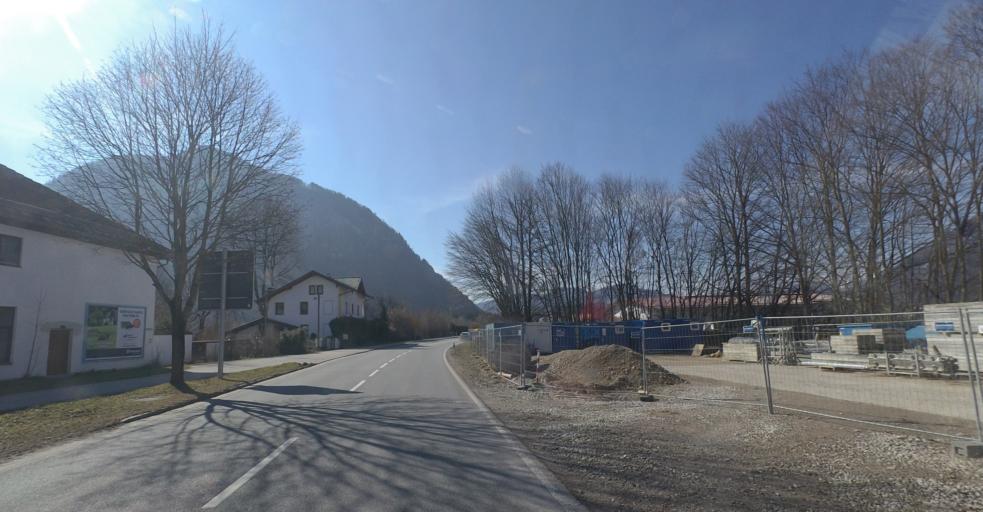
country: DE
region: Bavaria
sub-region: Upper Bavaria
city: Staudach-Egerndach
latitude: 47.7785
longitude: 12.4757
